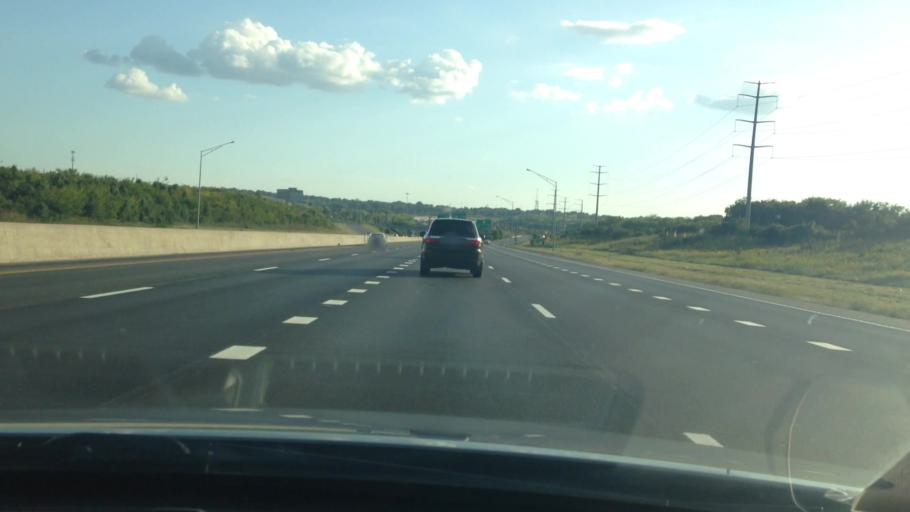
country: US
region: Missouri
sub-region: Jackson County
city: Grandview
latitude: 38.9574
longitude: -94.5272
